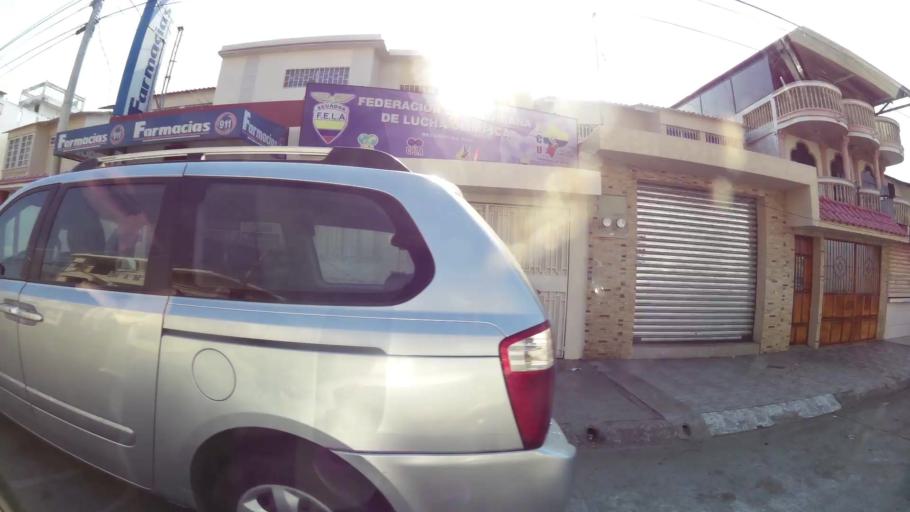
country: EC
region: Guayas
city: Guayaquil
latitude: -2.1492
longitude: -79.9092
